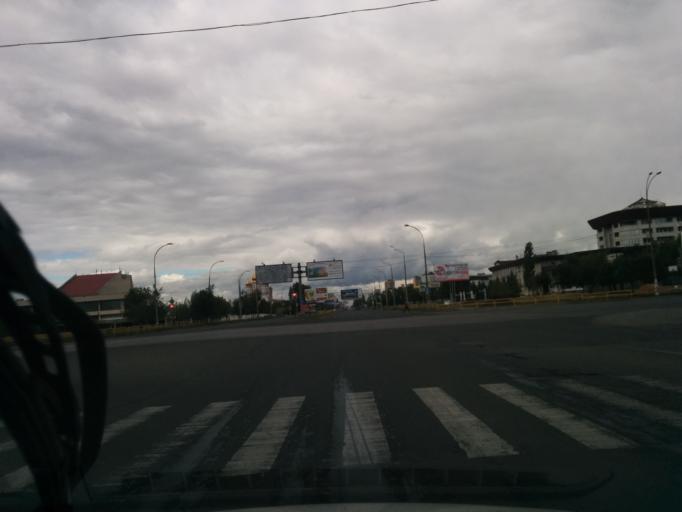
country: RU
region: Samara
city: Tol'yatti
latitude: 53.5145
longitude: 49.2782
